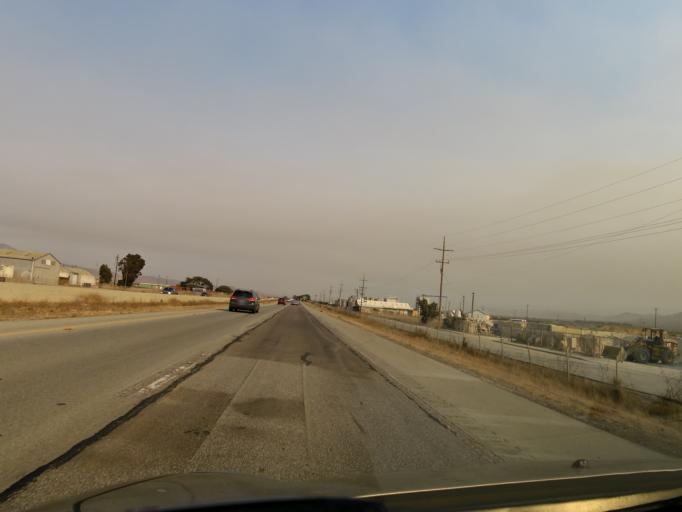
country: US
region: California
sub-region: Monterey County
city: Soledad
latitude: 36.4553
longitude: -121.3727
